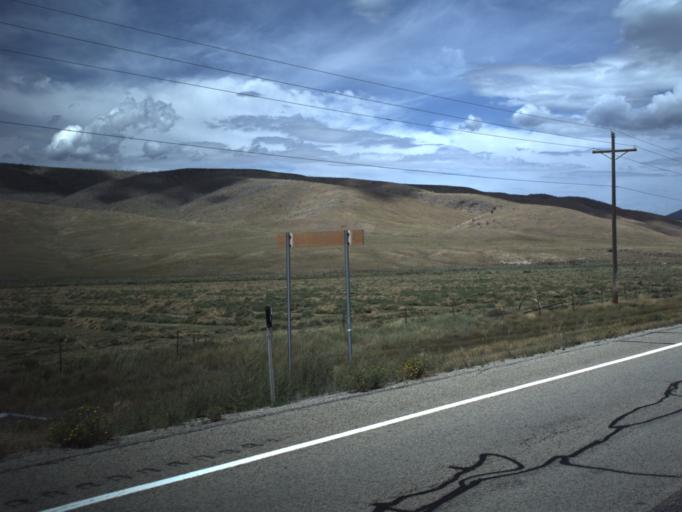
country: US
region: Utah
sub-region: Sanpete County
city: Fairview
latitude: 39.8064
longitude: -111.5039
